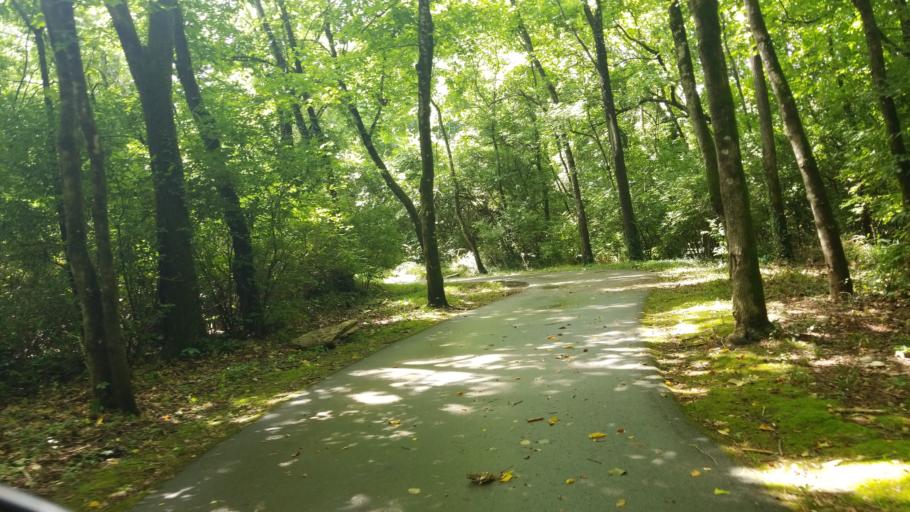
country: US
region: Tennessee
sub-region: Davidson County
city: Forest Hills
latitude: 36.0363
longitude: -86.8380
